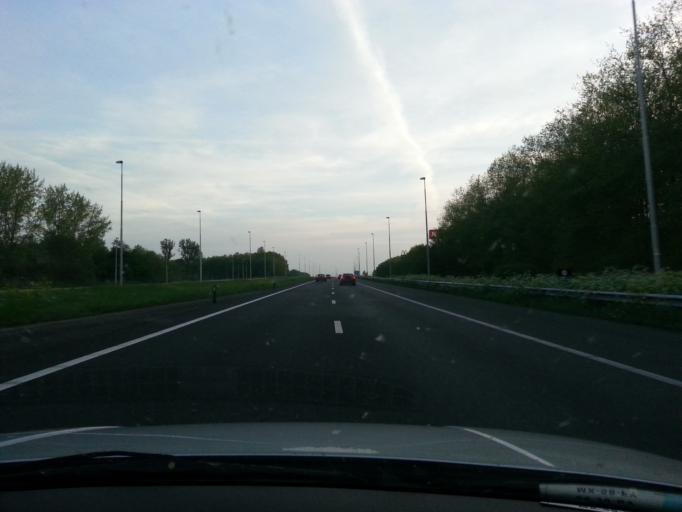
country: NL
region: Flevoland
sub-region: Gemeente Lelystad
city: Lelystad
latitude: 52.4855
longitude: 5.5137
